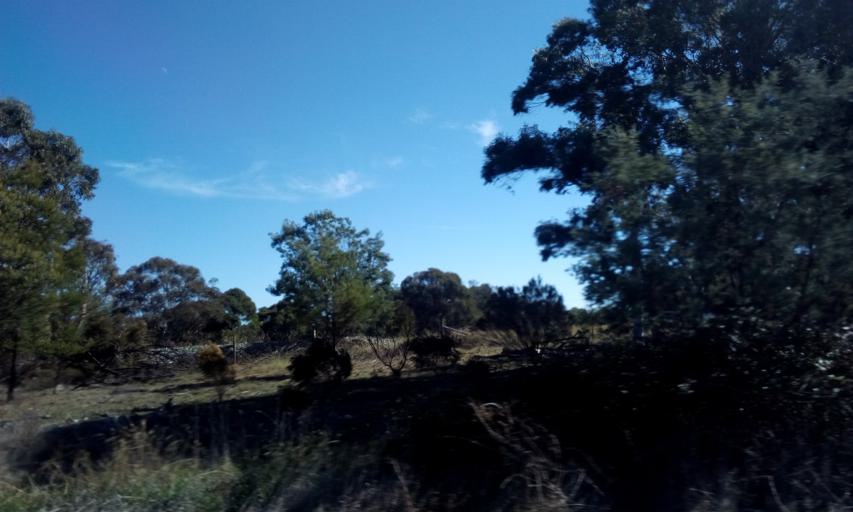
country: AU
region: New South Wales
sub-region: Yass Valley
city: Gundaroo
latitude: -35.1313
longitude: 149.3410
